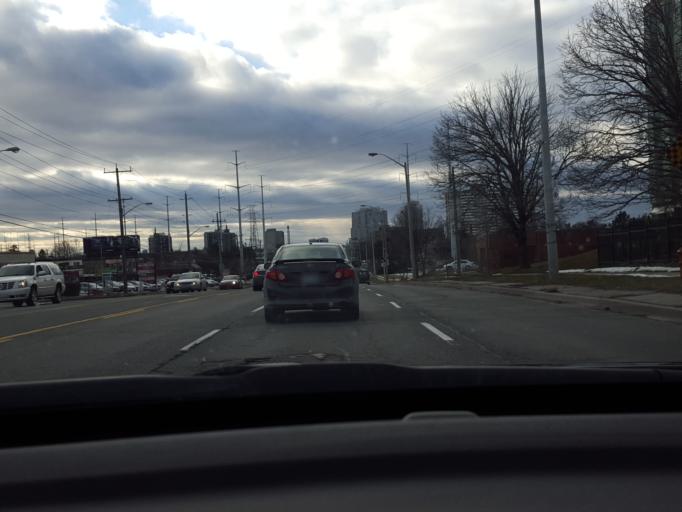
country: CA
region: Ontario
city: Scarborough
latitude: 43.7543
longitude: -79.2517
